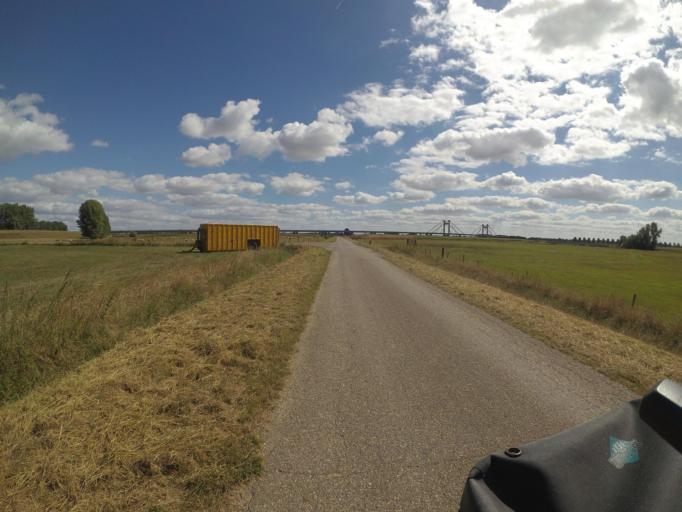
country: NL
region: Gelderland
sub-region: Gemeente Buren
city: Lienden
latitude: 51.8979
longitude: 5.4882
